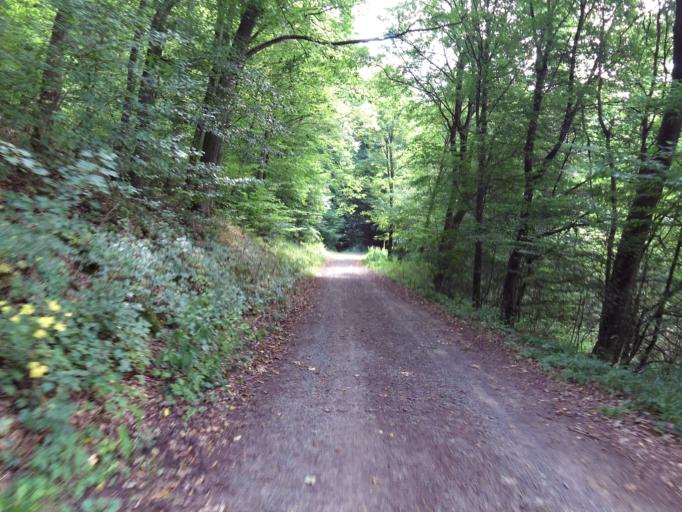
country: DE
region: Rheinland-Pfalz
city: Imsweiler
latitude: 49.6057
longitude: 7.8155
